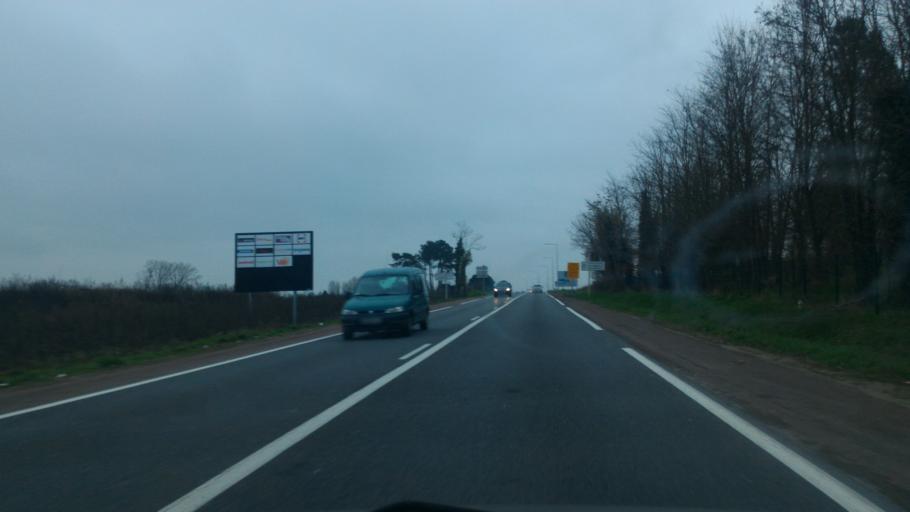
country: FR
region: Aquitaine
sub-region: Departement de la Gironde
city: Saint-Gervais
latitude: 45.0081
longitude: -0.4385
